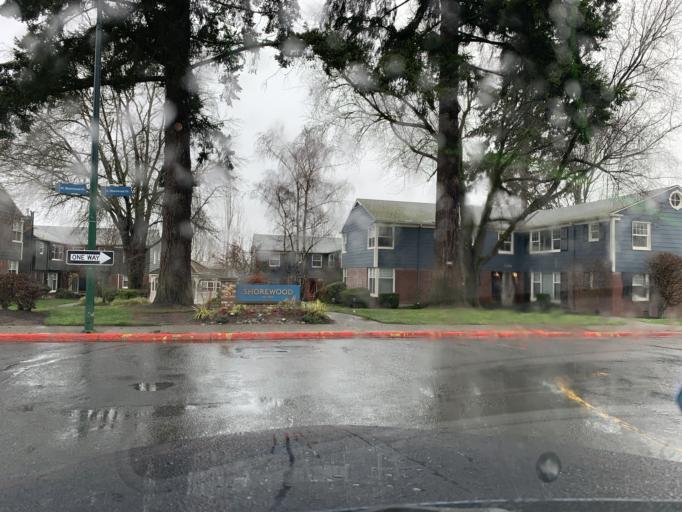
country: US
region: Washington
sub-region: King County
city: Mercer Island
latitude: 47.5791
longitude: -122.2218
